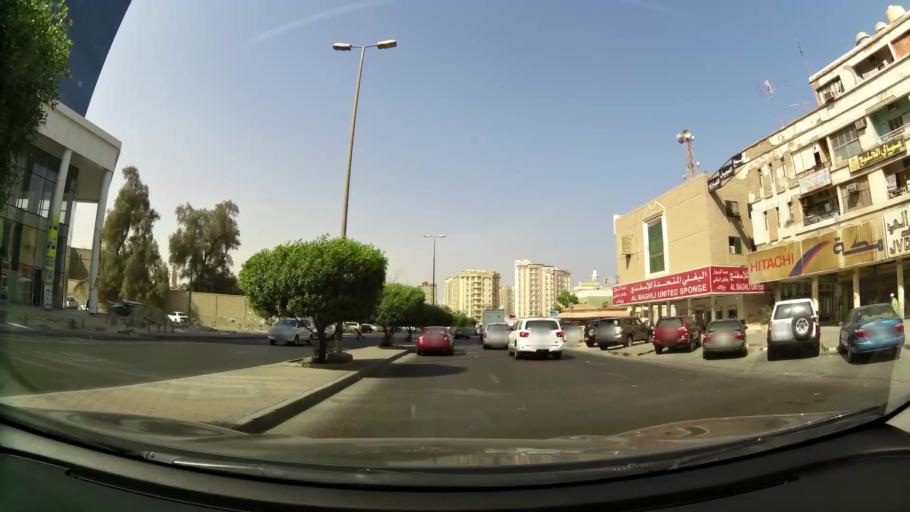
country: KW
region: Al Ahmadi
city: Al Fahahil
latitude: 29.0809
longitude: 48.1343
